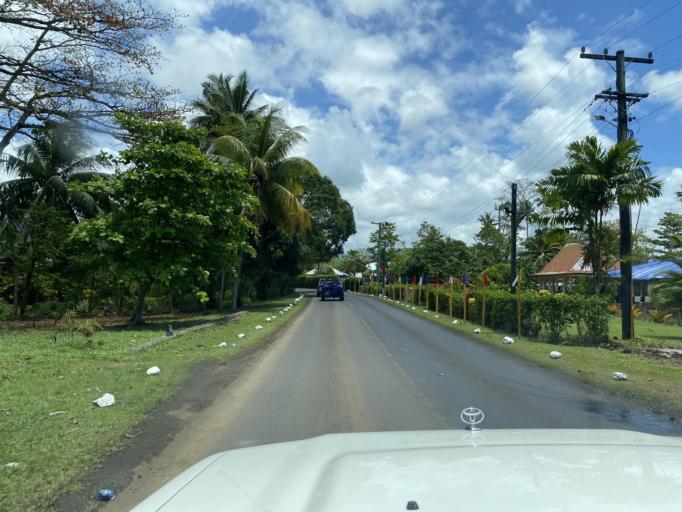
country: WS
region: Tuamasaga
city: Apia
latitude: -13.8501
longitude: -171.7795
